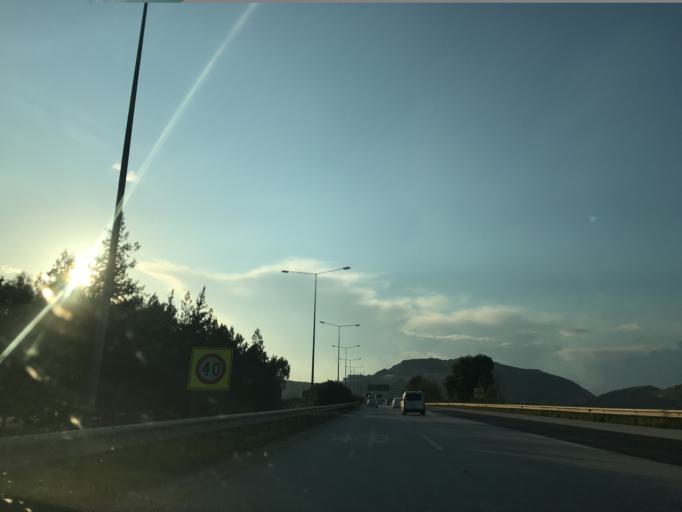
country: TR
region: Adana
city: Ceyhan
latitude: 36.9872
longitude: 35.7600
